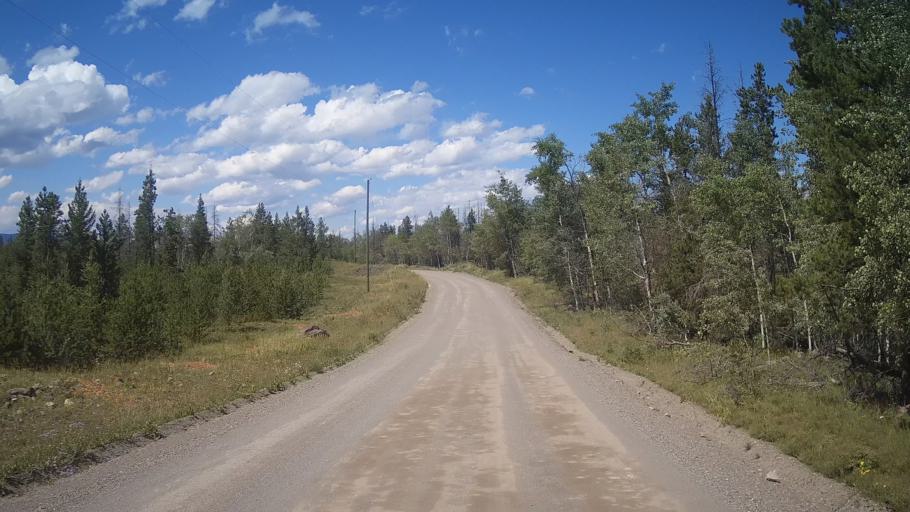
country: CA
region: British Columbia
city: Cache Creek
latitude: 51.2486
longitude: -121.6633
